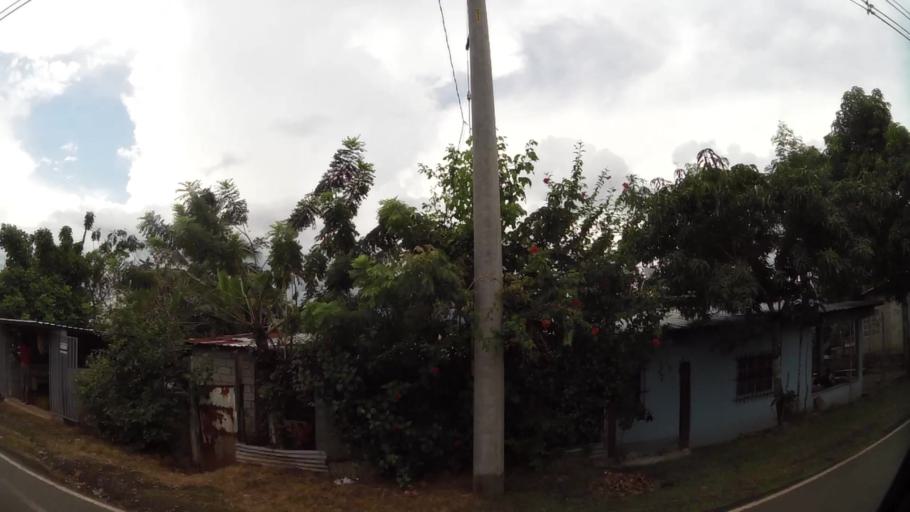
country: PA
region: Panama
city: Cabra Numero Uno
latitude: 9.1099
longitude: -79.3627
